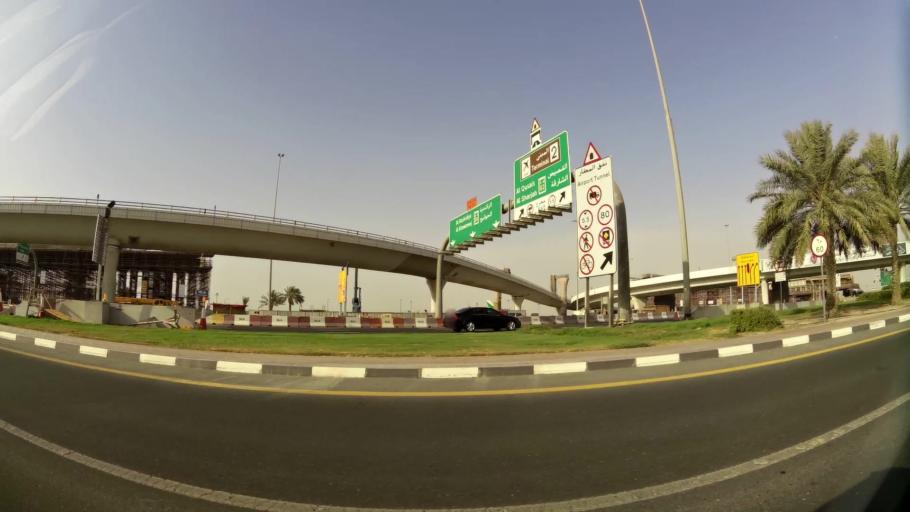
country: AE
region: Ash Shariqah
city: Sharjah
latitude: 25.2370
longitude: 55.3773
